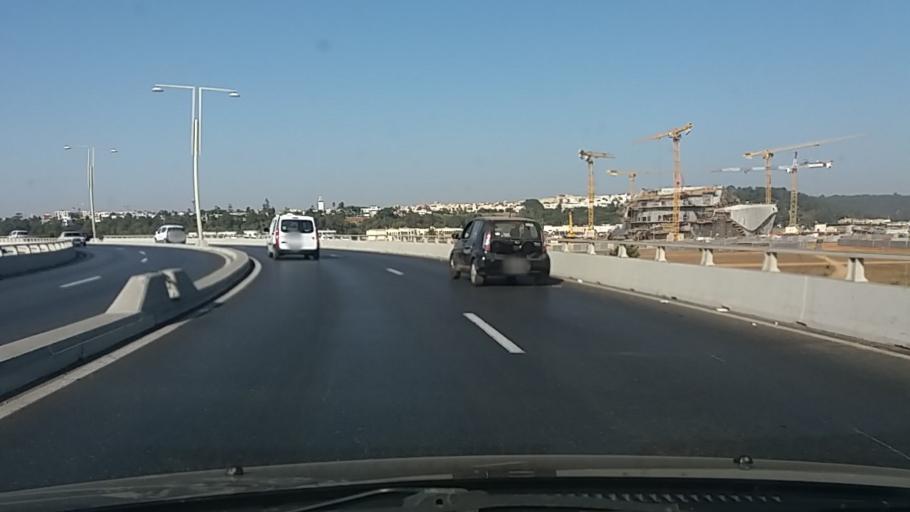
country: MA
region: Rabat-Sale-Zemmour-Zaer
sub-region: Rabat
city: Rabat
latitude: 34.0250
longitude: -6.8203
